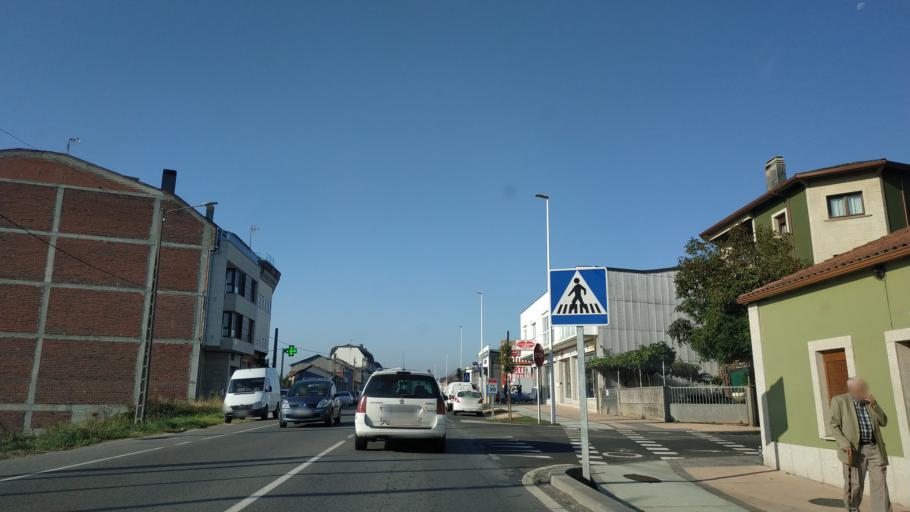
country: ES
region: Galicia
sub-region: Provincia da Coruna
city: Carballo
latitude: 43.2244
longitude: -8.6808
